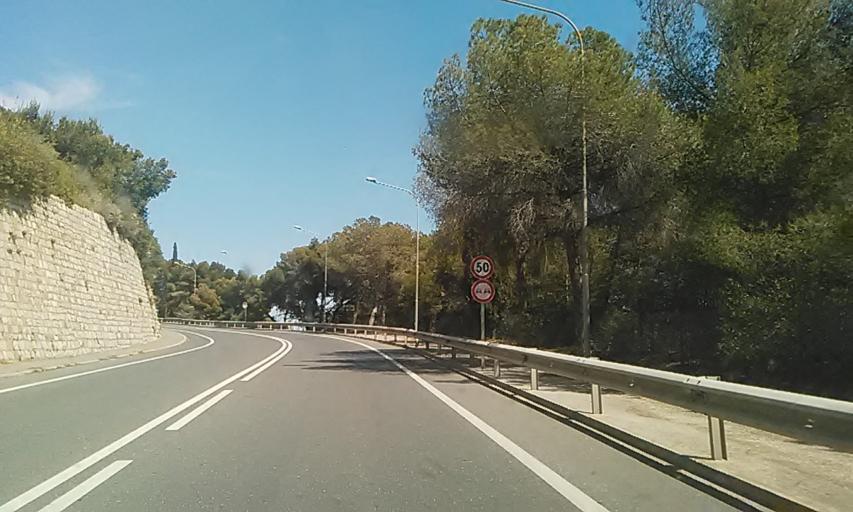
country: IT
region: Liguria
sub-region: Provincia di Savona
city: Marina di Andora
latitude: 43.9526
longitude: 8.1639
